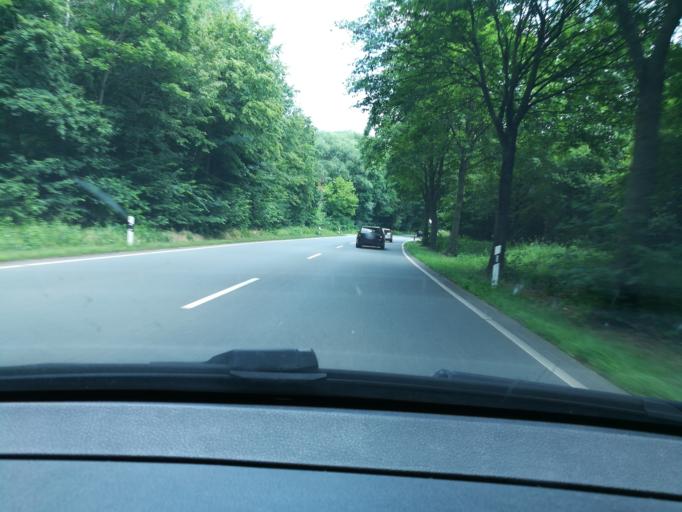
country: DE
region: North Rhine-Westphalia
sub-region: Regierungsbezirk Detmold
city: Minden
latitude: 52.3108
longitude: 8.9699
